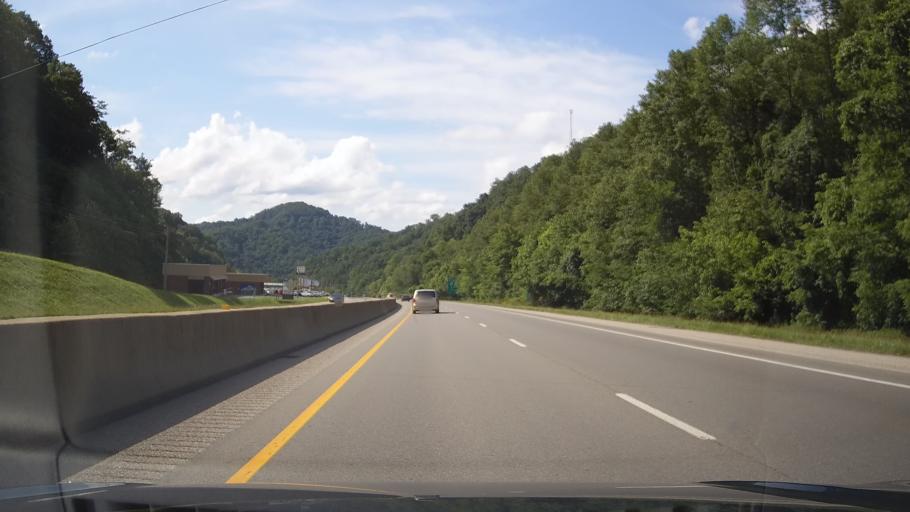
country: US
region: Kentucky
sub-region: Floyd County
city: Prestonsburg
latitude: 37.6267
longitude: -82.7382
